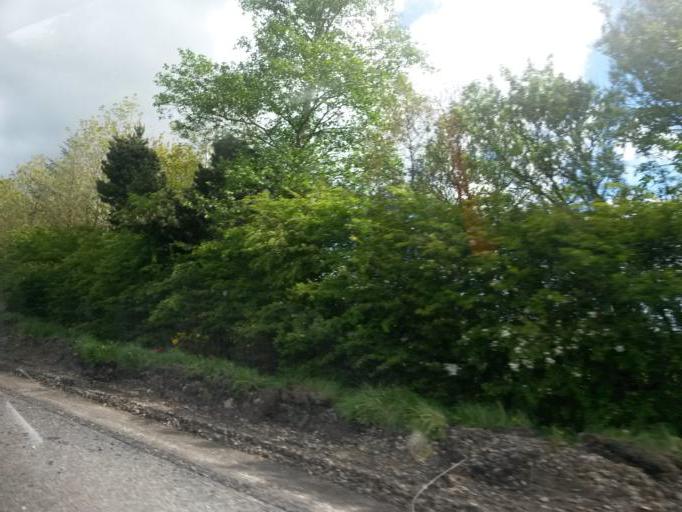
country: IE
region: Leinster
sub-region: Loch Garman
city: Castlebridge
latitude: 52.3880
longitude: -6.5184
